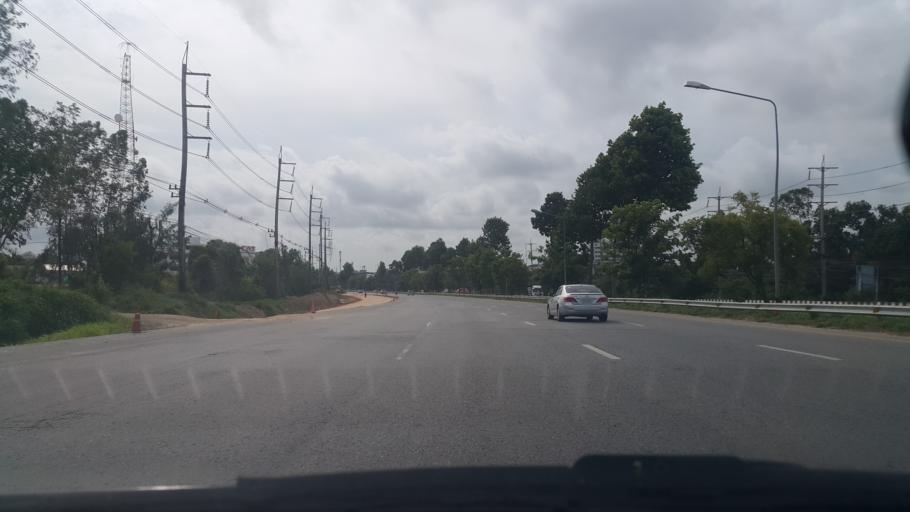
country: TH
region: Rayong
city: Rayong
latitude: 12.6900
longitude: 101.2958
